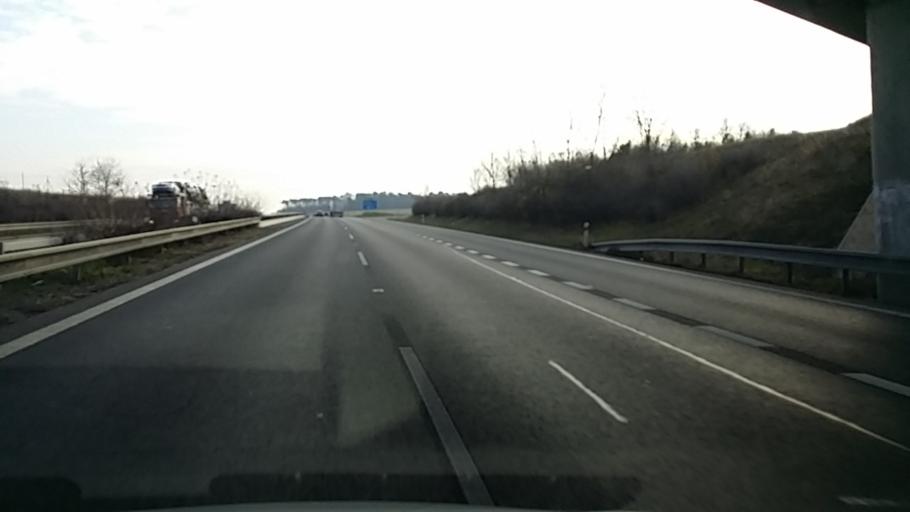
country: CZ
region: Ustecky
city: Roudnice nad Labem
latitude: 50.3956
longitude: 14.2273
